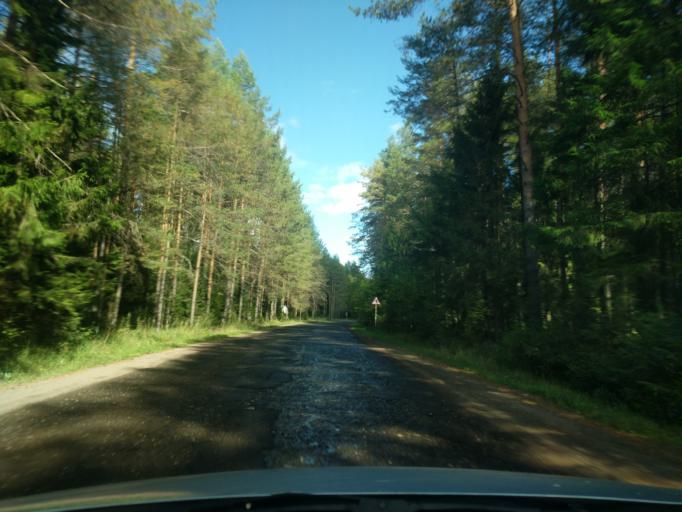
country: RU
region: Kirov
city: Kirovo-Chepetsk
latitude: 58.6047
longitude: 49.9152
